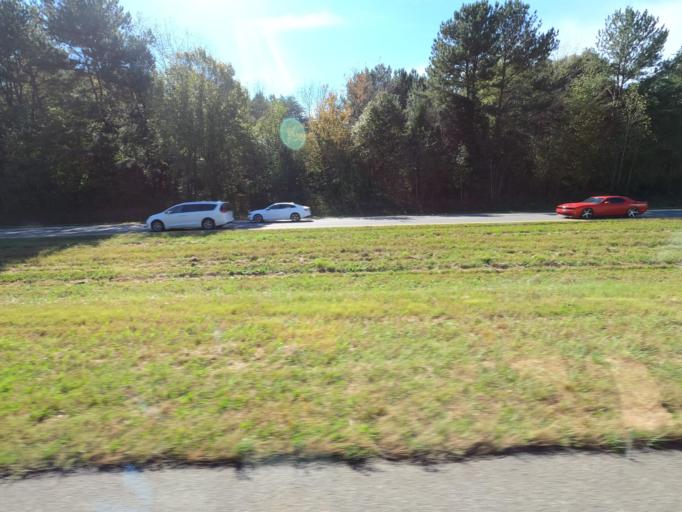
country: US
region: Tennessee
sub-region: Dickson County
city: Burns
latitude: 36.0190
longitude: -87.2375
